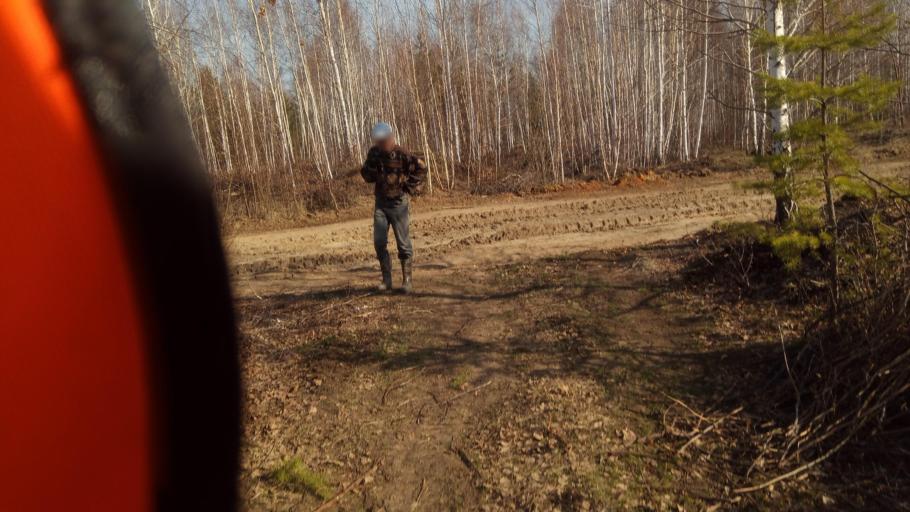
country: RU
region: Chelyabinsk
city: Sargazy
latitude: 55.1224
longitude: 61.2437
